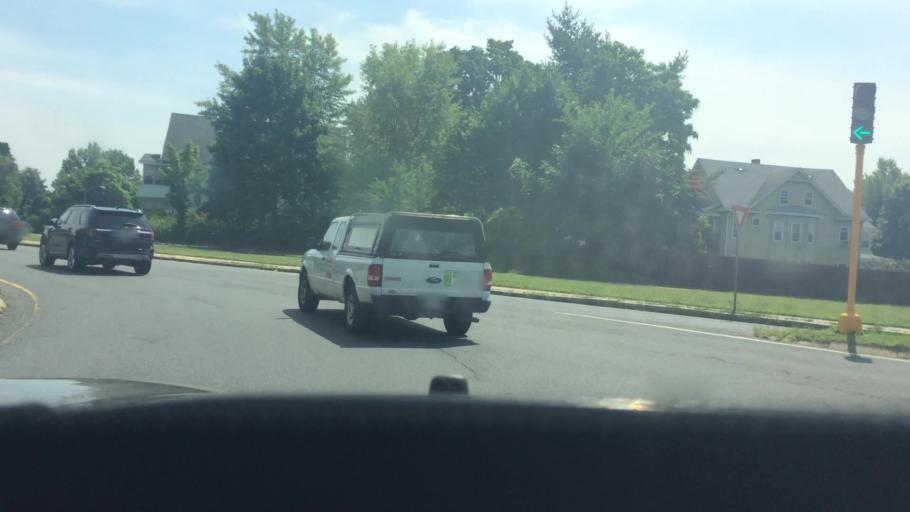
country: US
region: Massachusetts
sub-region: Hampden County
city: Springfield
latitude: 42.1175
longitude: -72.5846
